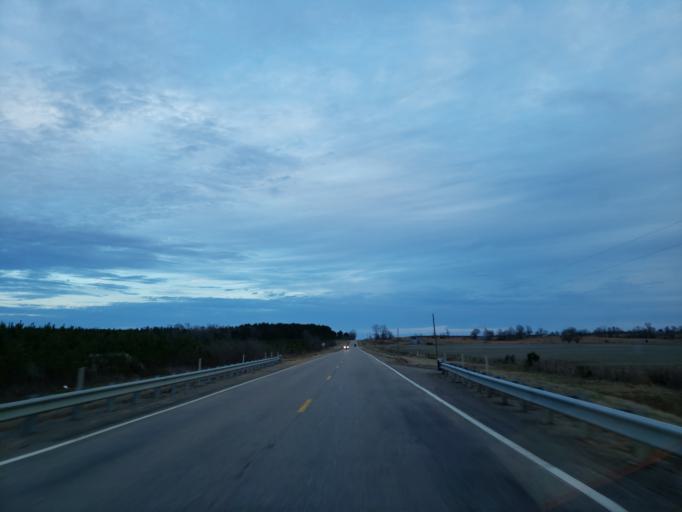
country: US
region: Mississippi
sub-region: Kemper County
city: De Kalb
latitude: 32.8309
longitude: -88.3961
